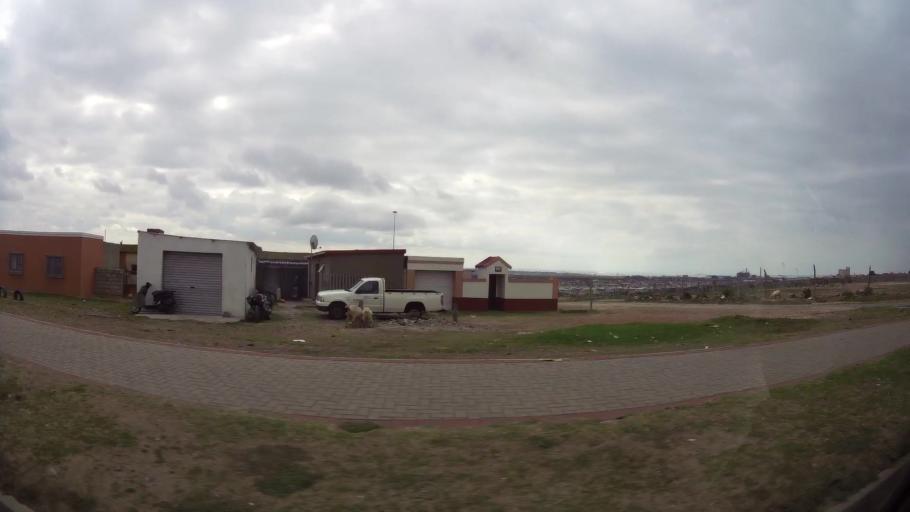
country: ZA
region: Eastern Cape
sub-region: Nelson Mandela Bay Metropolitan Municipality
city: Port Elizabeth
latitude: -33.8917
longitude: 25.6011
